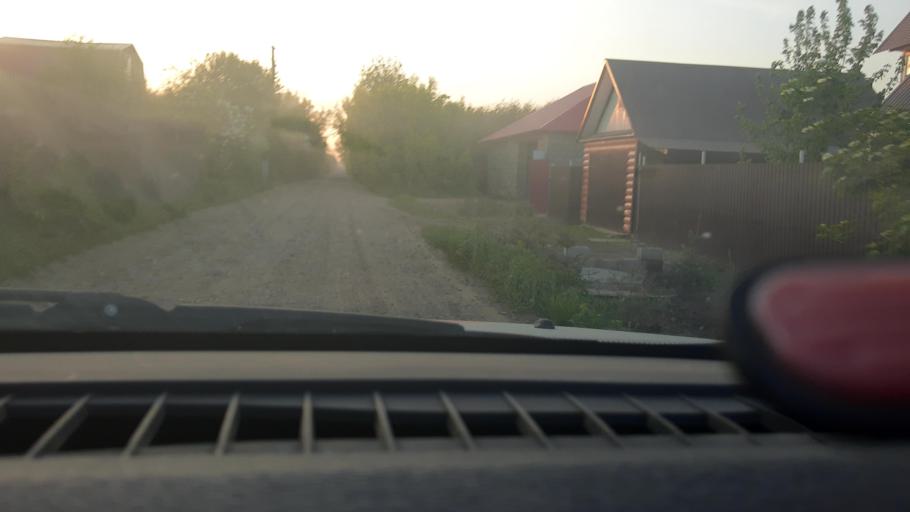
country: RU
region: Bashkortostan
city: Ufa
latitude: 54.5512
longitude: 55.9323
